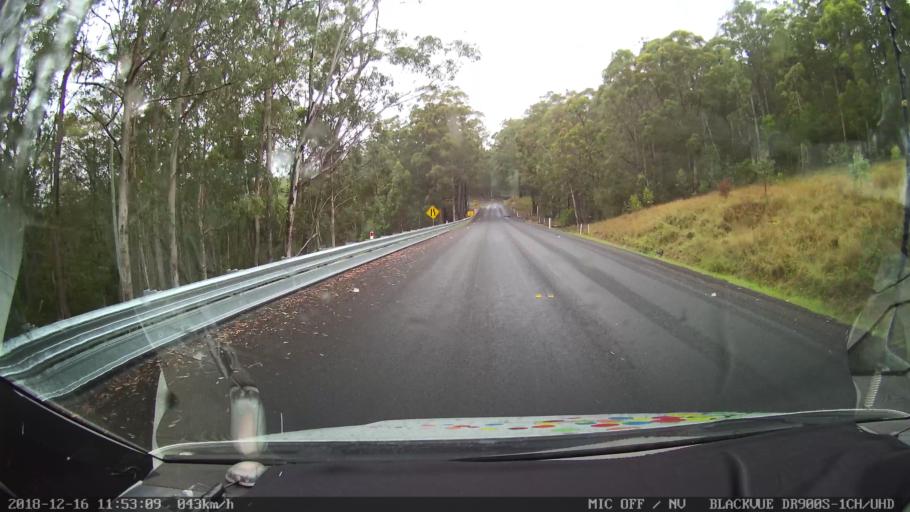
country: AU
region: New South Wales
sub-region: Tenterfield Municipality
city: Carrolls Creek
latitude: -28.9035
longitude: 152.2776
